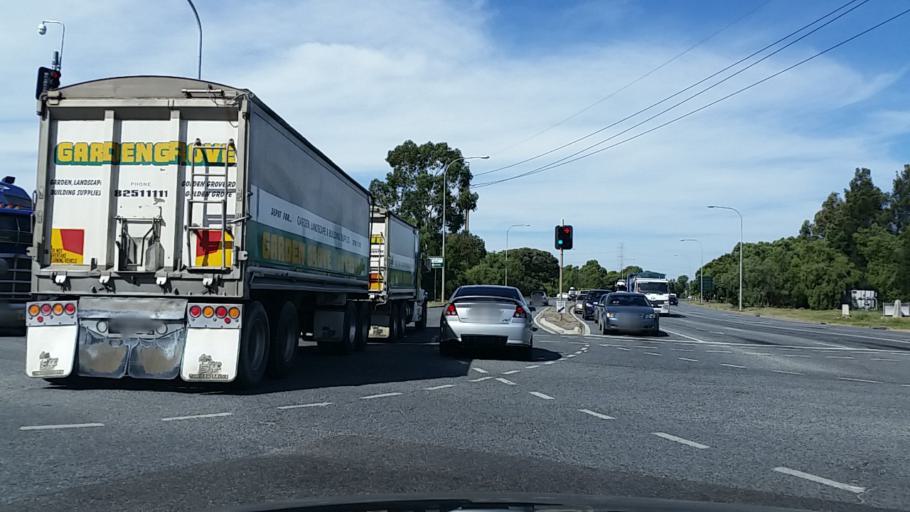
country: AU
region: South Australia
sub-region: Port Adelaide Enfield
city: Enfield
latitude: -34.8276
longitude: 138.5985
